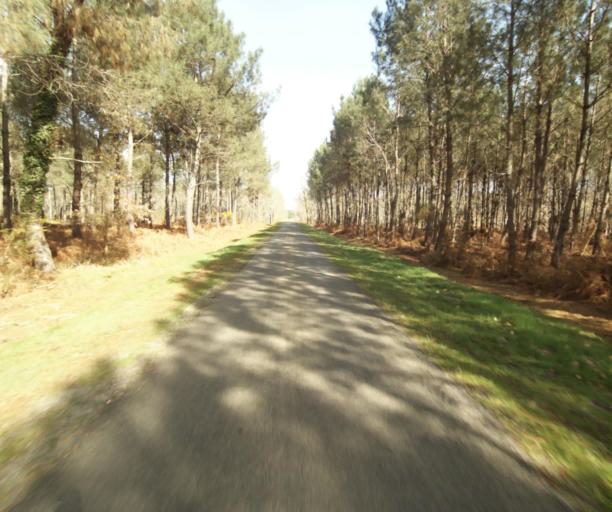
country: FR
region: Aquitaine
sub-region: Departement des Landes
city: Roquefort
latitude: 44.1540
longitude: -0.2294
